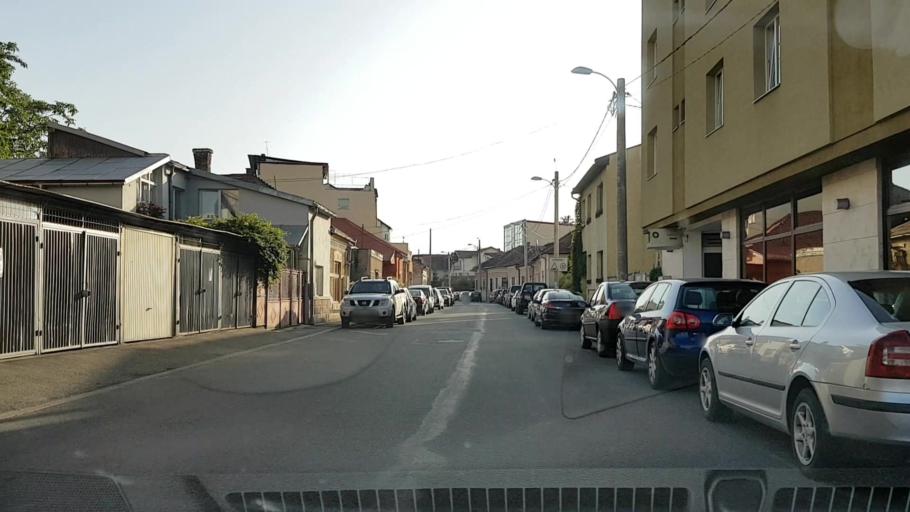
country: RO
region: Cluj
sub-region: Municipiul Cluj-Napoca
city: Cluj-Napoca
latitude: 46.7703
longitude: 23.6089
